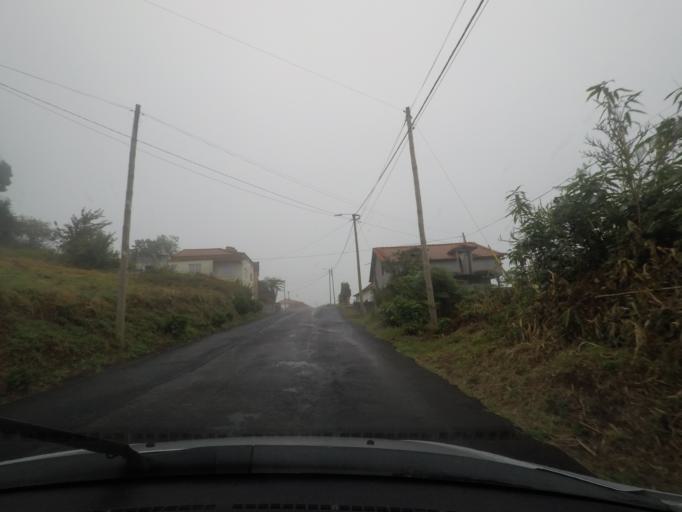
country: PT
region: Madeira
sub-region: Santana
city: Santana
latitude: 32.7967
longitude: -16.8774
